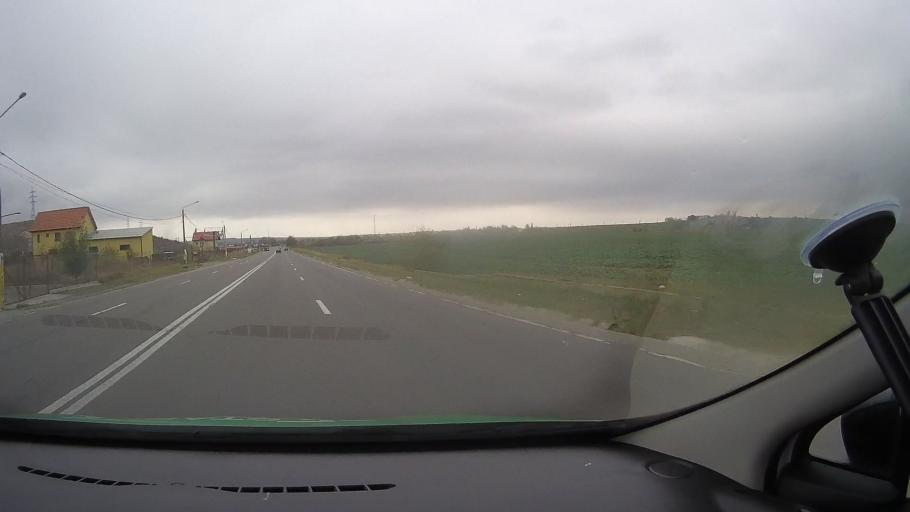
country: RO
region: Constanta
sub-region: Oras Murfatlar
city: Murfatlar
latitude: 44.1700
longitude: 28.4363
